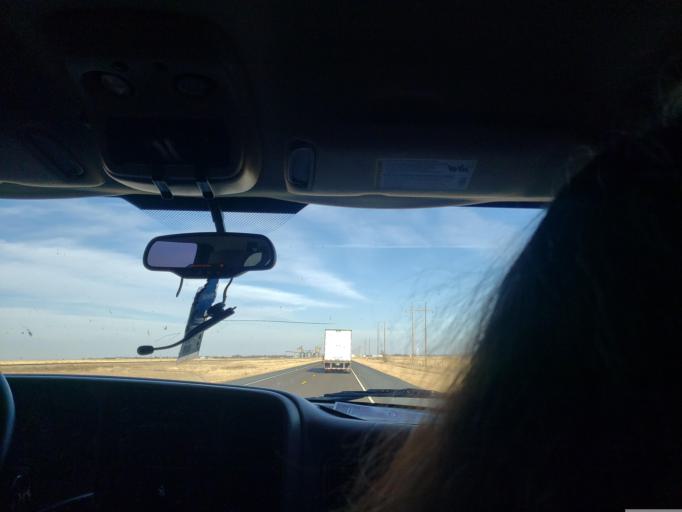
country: US
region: Oklahoma
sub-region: Texas County
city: Goodwell
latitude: 36.4856
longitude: -101.8119
